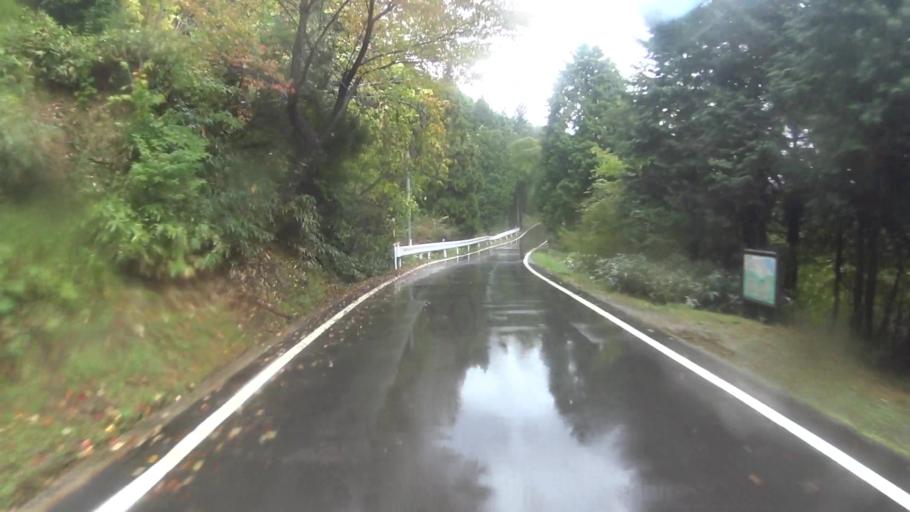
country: JP
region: Kyoto
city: Miyazu
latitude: 35.4722
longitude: 135.1550
